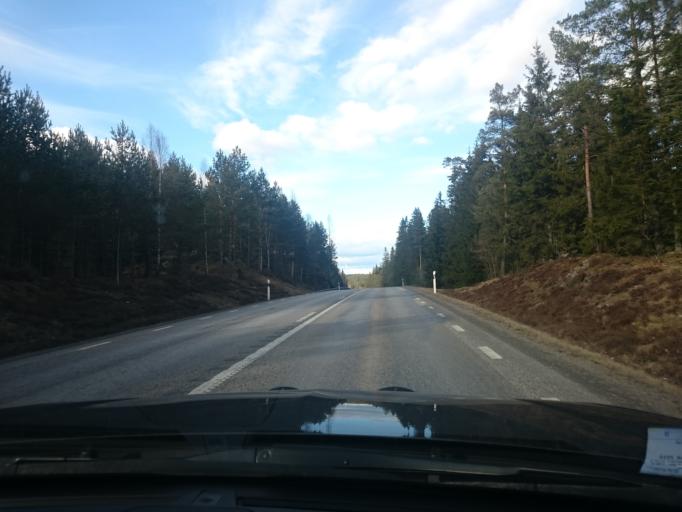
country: SE
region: Joenkoeping
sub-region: Vetlanda Kommun
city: Vetlanda
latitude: 57.3413
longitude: 15.1151
